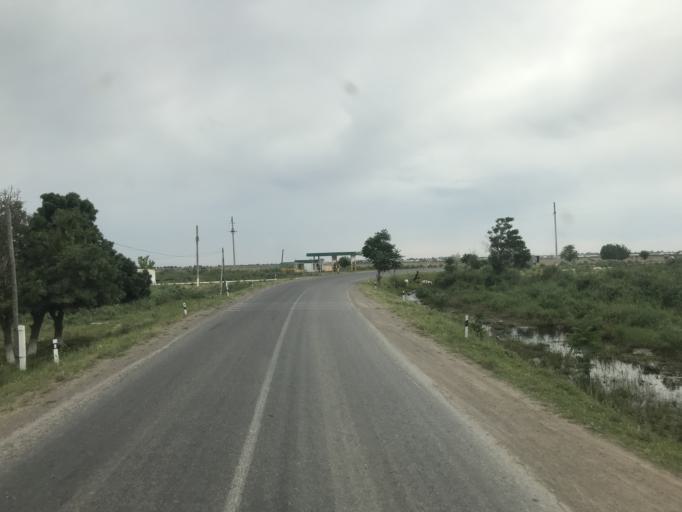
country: KZ
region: Ongtustik Qazaqstan
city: Asykata
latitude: 40.9109
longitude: 68.3926
